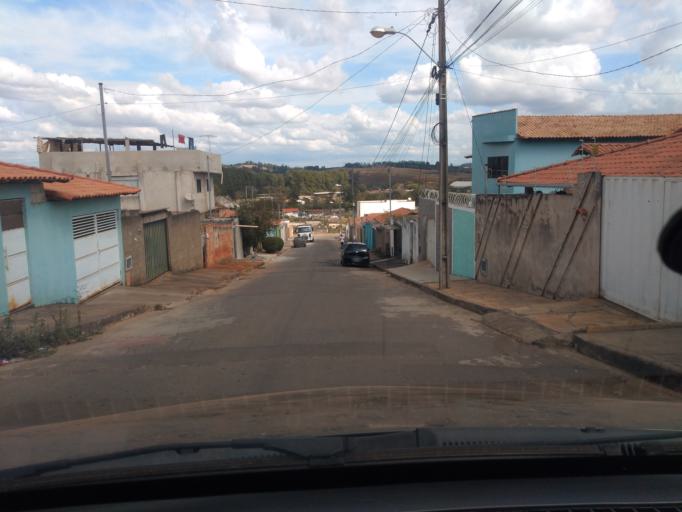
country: BR
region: Minas Gerais
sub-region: Tres Coracoes
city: Tres Coracoes
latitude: -21.6962
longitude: -45.2410
